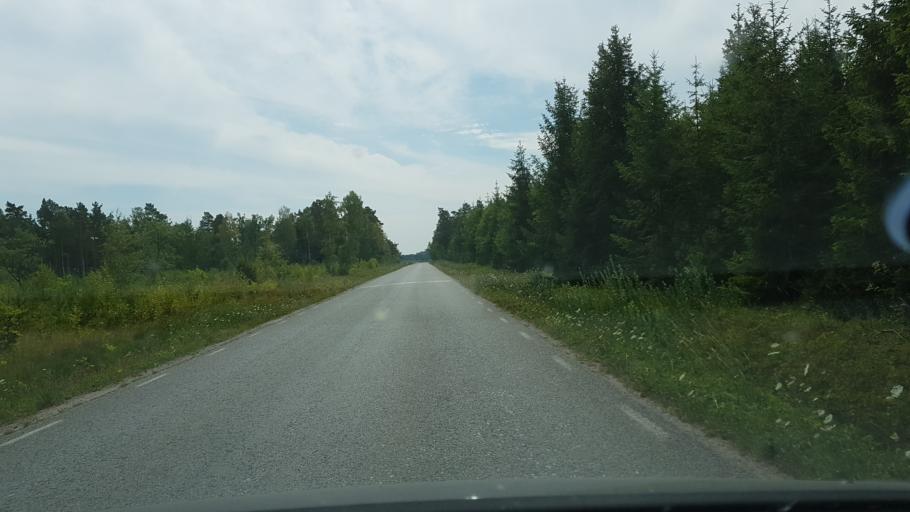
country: SE
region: Gotland
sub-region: Gotland
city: Visby
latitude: 57.7121
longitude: 18.5076
